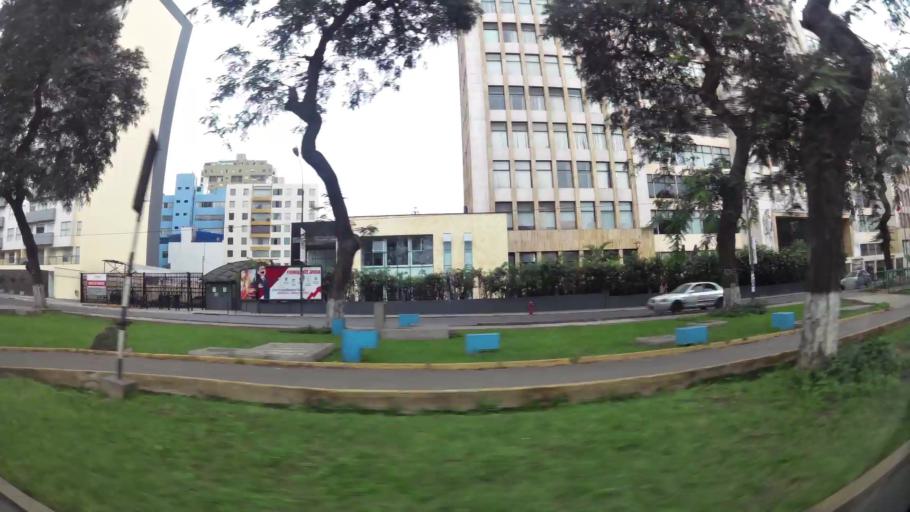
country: PE
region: Lima
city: Lima
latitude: -12.0711
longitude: -77.0408
